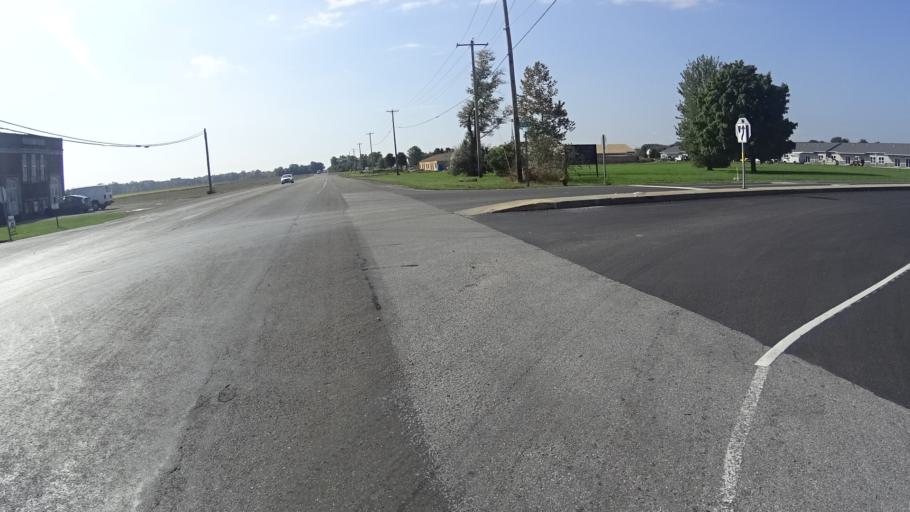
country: US
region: Indiana
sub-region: Madison County
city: Ingalls
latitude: 39.9879
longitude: -85.8432
